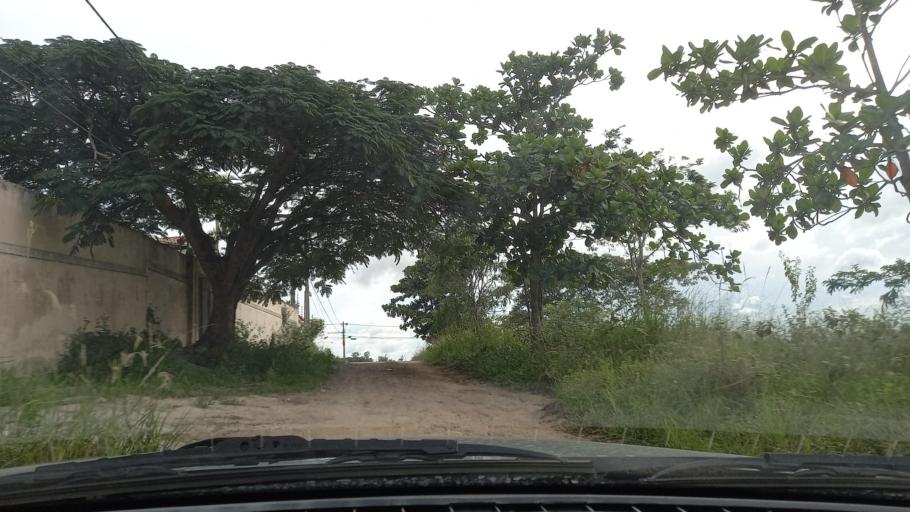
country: BR
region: Pernambuco
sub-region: Gravata
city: Gravata
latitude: -8.2031
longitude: -35.5472
